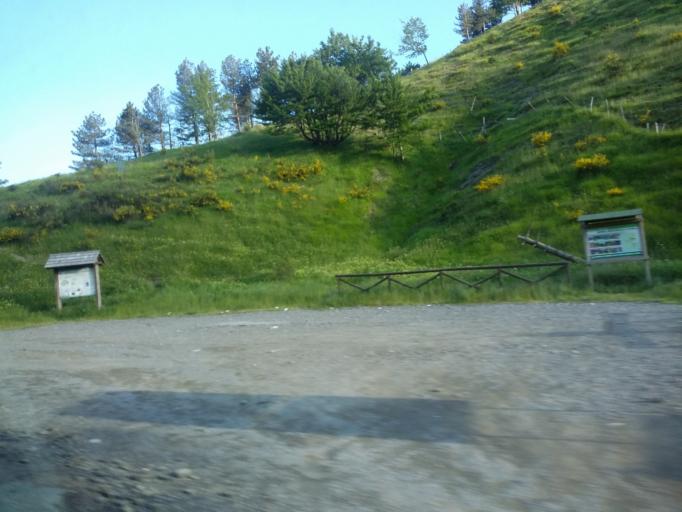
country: IT
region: Liguria
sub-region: Provincia di Genova
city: Lorsica
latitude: 44.4630
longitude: 9.3348
